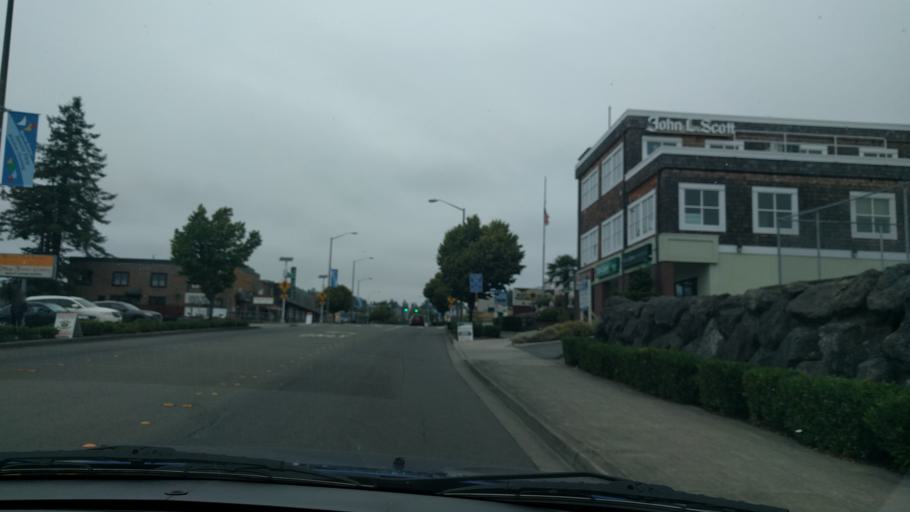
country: US
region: Washington
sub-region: King County
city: Des Moines
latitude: 47.3998
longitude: -122.3245
